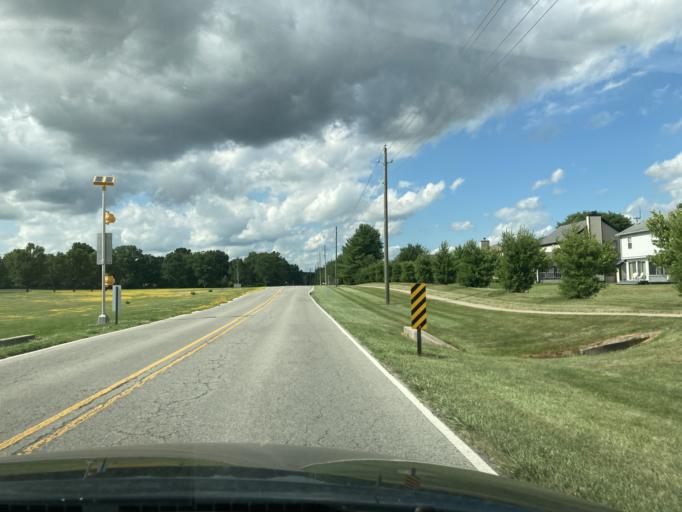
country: US
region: Indiana
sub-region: Marion County
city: Meridian Hills
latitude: 39.8741
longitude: -86.2221
